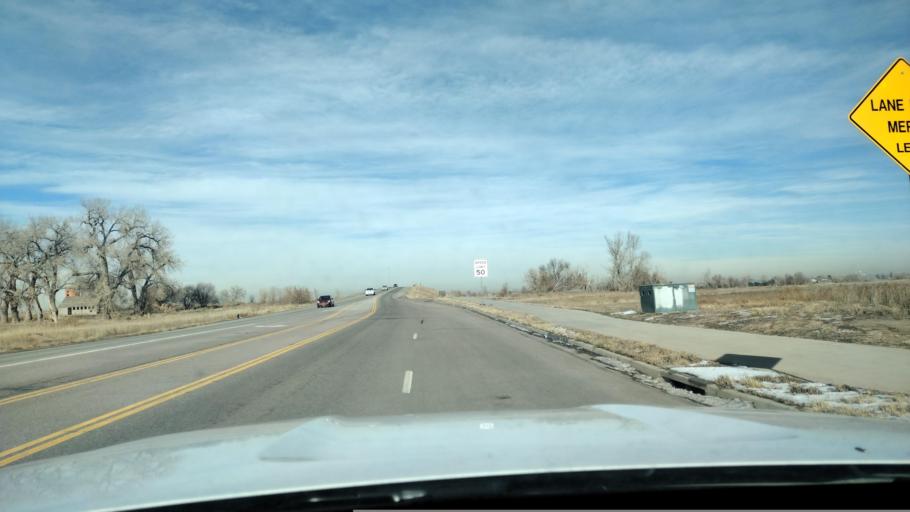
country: US
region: Colorado
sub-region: Adams County
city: Brighton
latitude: 39.9245
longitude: -104.8183
